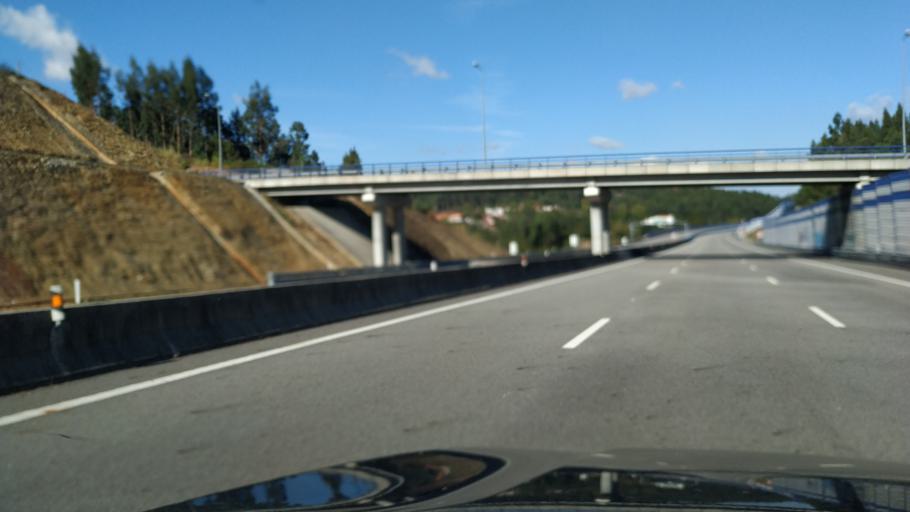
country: PT
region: Porto
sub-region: Vila Nova de Gaia
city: Olival
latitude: 41.0686
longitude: -8.5335
